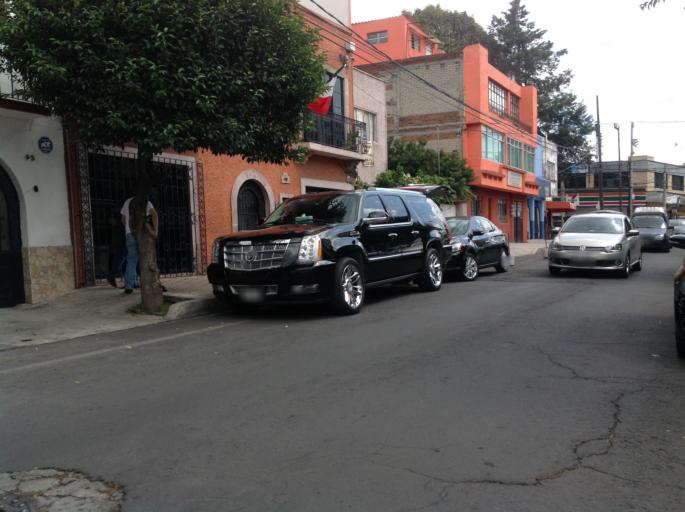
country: MX
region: Mexico City
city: Azcapotzalco
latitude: 19.4656
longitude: -99.1810
